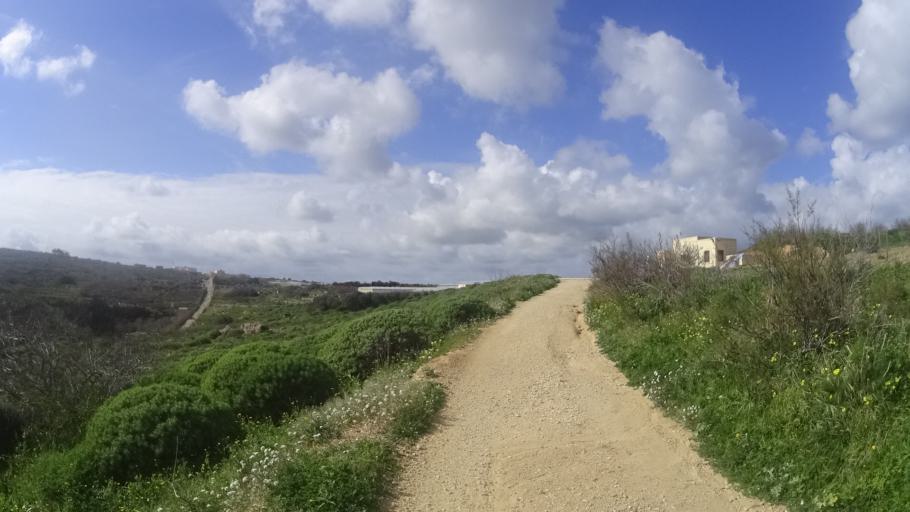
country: MT
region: Il-Qala
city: Qala
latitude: 36.0530
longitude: 14.3070
